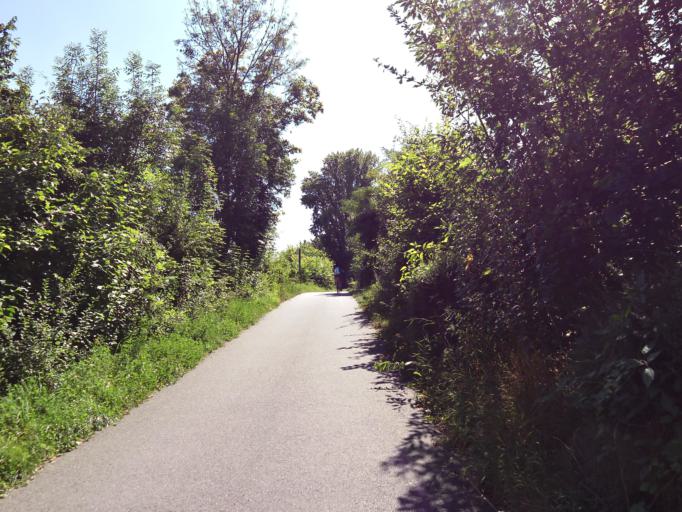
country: DE
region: Rheinland-Pfalz
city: Mainz
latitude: 49.9869
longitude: 8.2979
